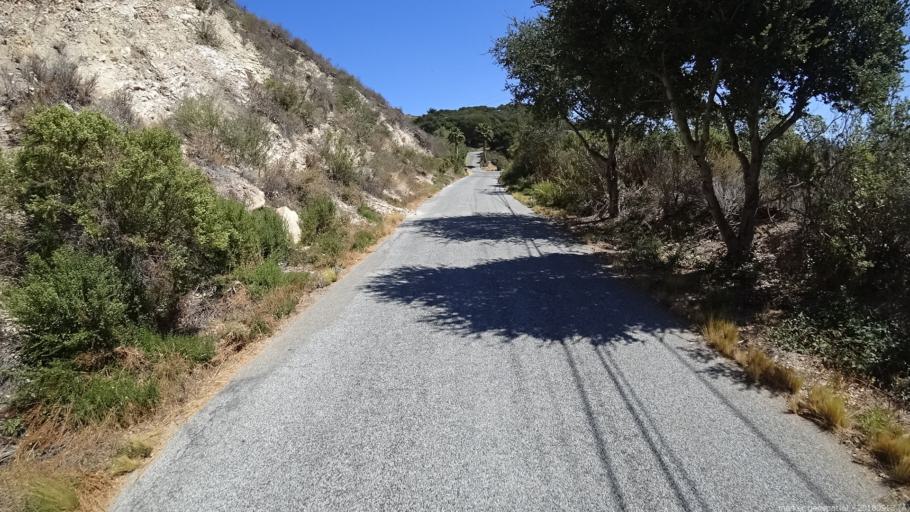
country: US
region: California
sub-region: Monterey County
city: Carmel Valley Village
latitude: 36.5154
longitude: -121.7725
